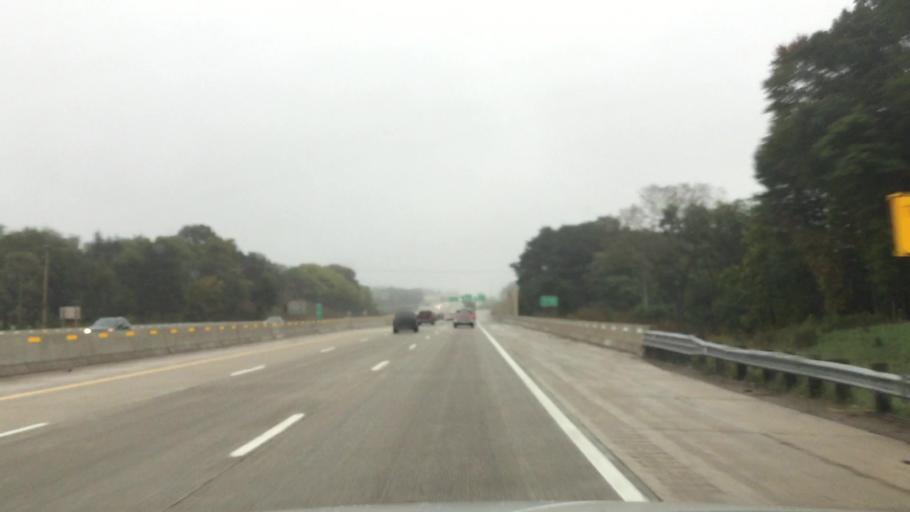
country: US
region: Michigan
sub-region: Kalamazoo County
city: Westwood
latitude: 42.2378
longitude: -85.6503
